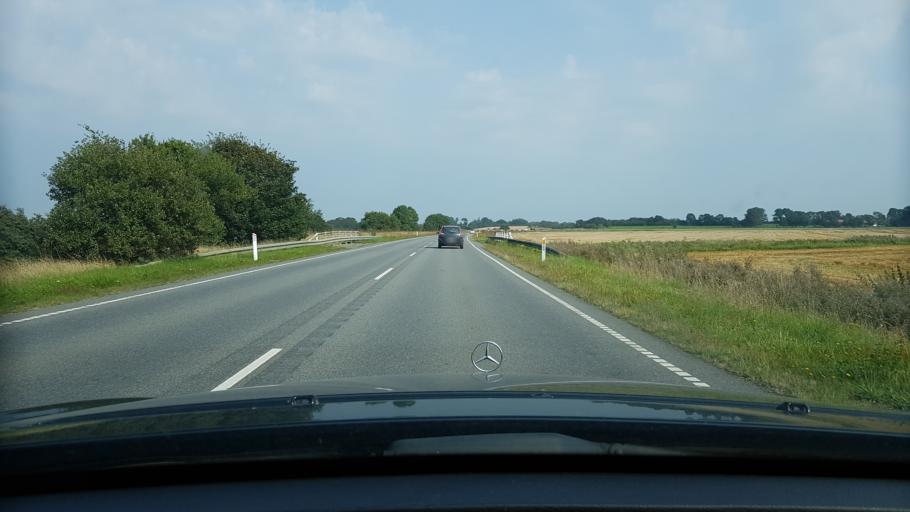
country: DK
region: North Denmark
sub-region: Alborg Kommune
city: Klarup
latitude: 57.0225
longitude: 10.0261
